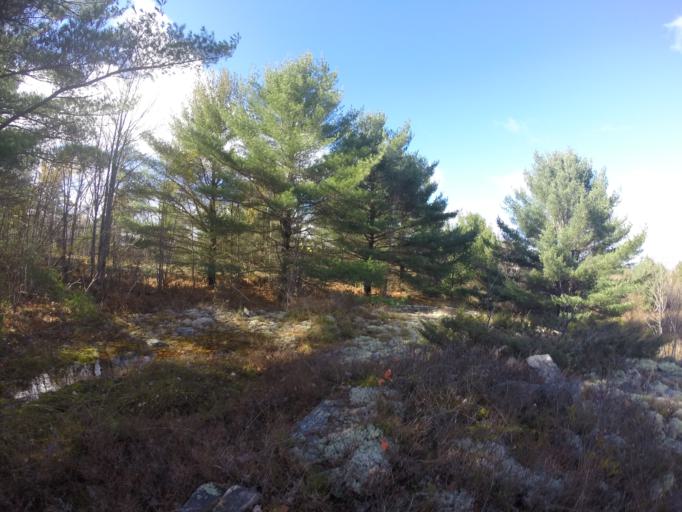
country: CA
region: Ontario
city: Greater Sudbury
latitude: 46.1089
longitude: -80.6514
